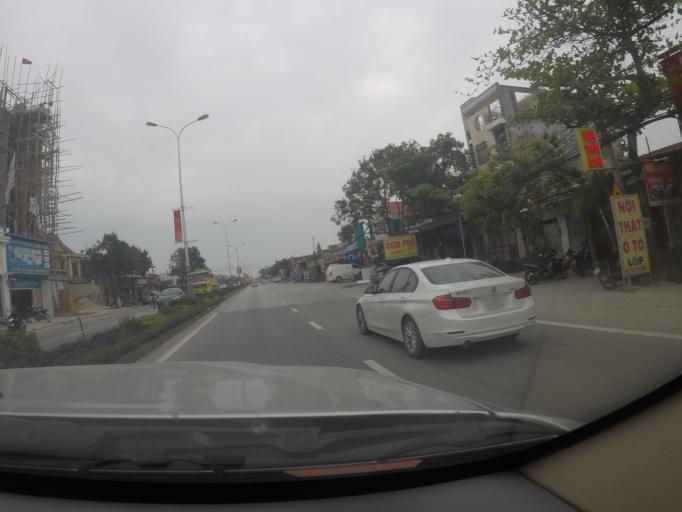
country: VN
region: Nghe An
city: Dien Chau
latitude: 18.9693
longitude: 105.6008
